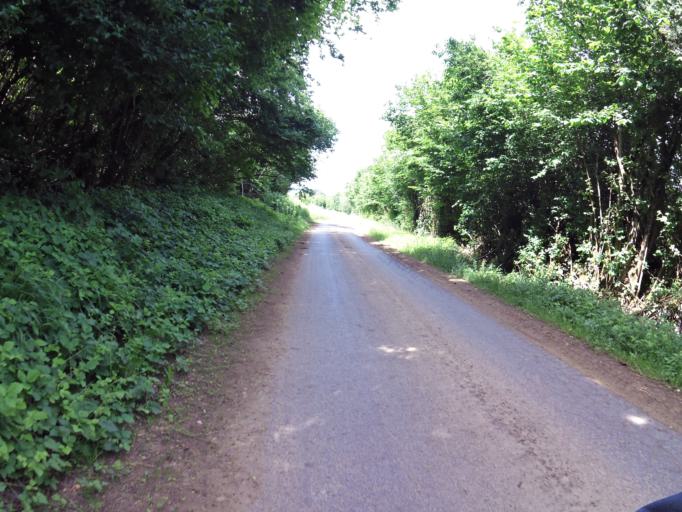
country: FR
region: Champagne-Ardenne
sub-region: Departement des Ardennes
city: Mouzon
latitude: 49.5303
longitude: 5.0922
